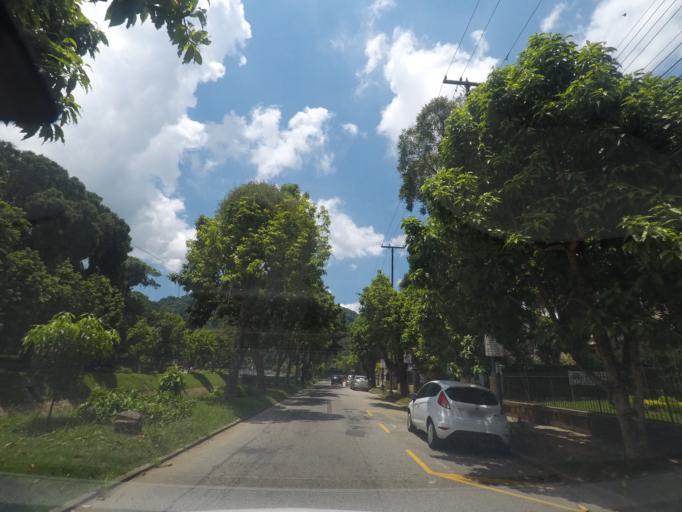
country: BR
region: Rio de Janeiro
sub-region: Petropolis
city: Petropolis
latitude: -22.5071
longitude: -43.1803
